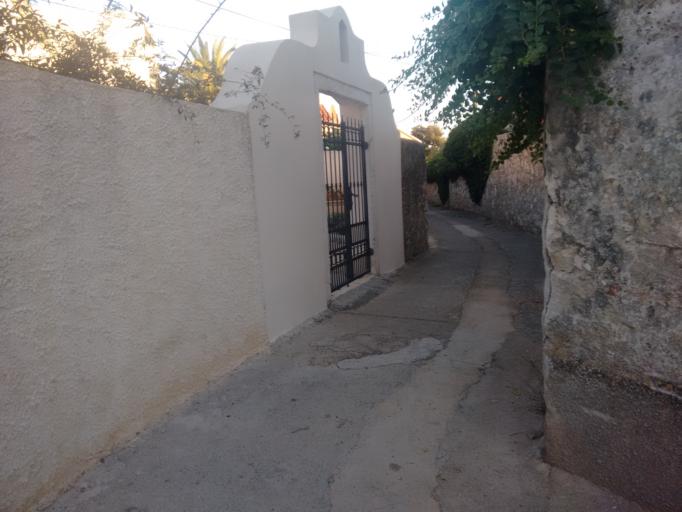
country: HR
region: Licko-Senjska
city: Novalja
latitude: 44.3754
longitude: 14.6967
